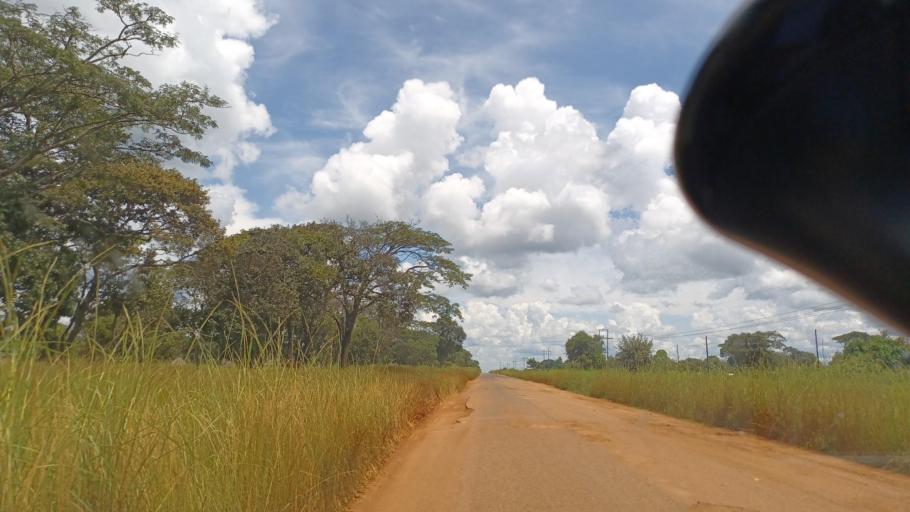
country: ZM
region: North-Western
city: Solwezi
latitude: -12.4924
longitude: 26.1886
